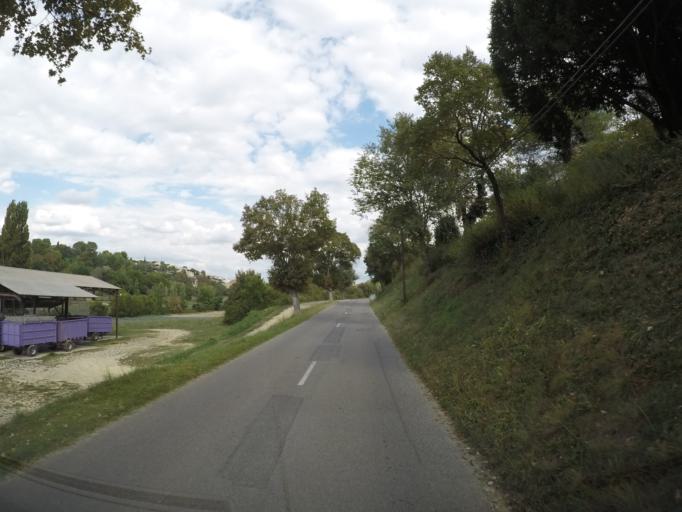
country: FR
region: Provence-Alpes-Cote d'Azur
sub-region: Departement des Alpes-de-Haute-Provence
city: Valensole
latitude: 43.8299
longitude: 5.9784
